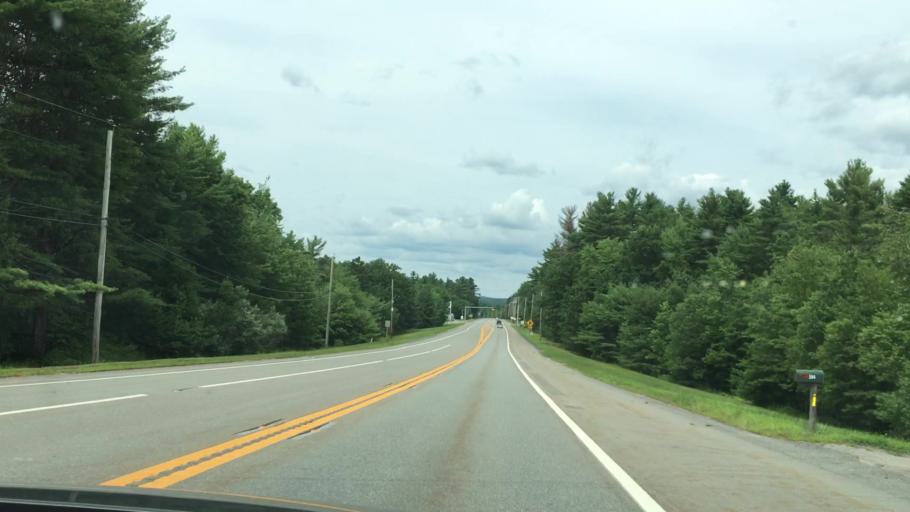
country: US
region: Massachusetts
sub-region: Worcester County
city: Winchendon
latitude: 42.6370
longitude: -72.0057
